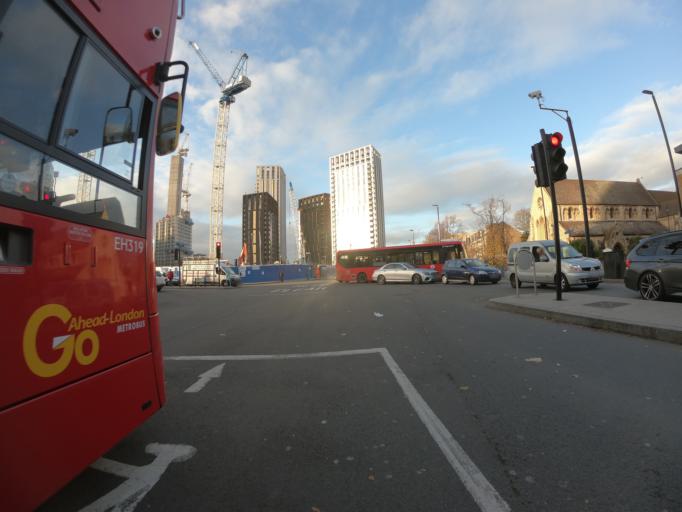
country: GB
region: England
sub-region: Greater London
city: Blackheath
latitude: 51.4636
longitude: -0.0106
